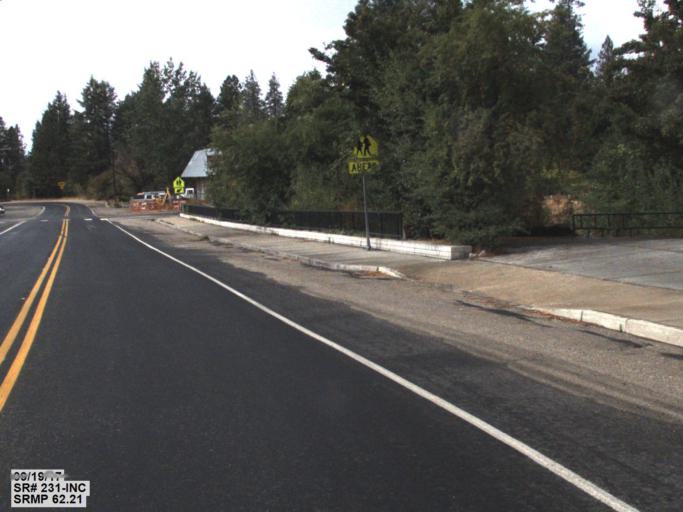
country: US
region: Washington
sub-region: Stevens County
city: Chewelah
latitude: 48.0576
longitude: -117.7414
